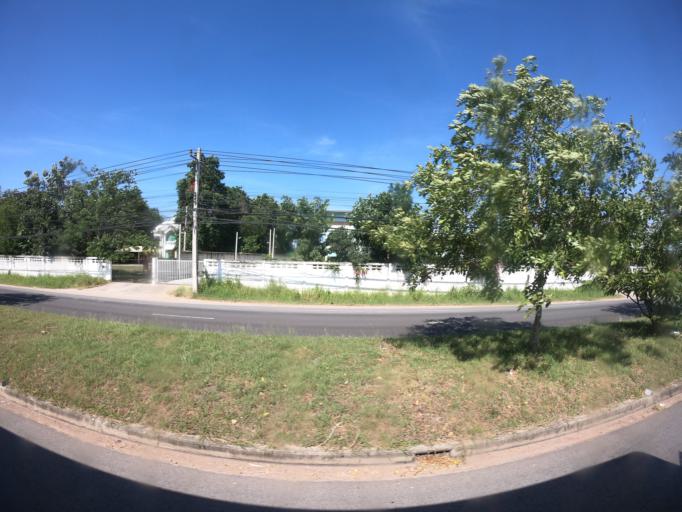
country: TH
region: Nakhon Ratchasima
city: Nakhon Ratchasima
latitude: 15.0118
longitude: 102.1267
